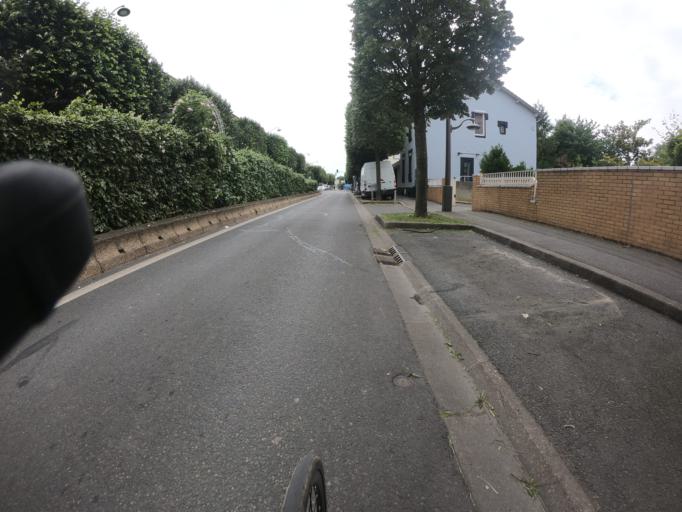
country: FR
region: Ile-de-France
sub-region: Departement du Val-de-Marne
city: Chevilly-Larue
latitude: 48.7701
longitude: 2.3643
